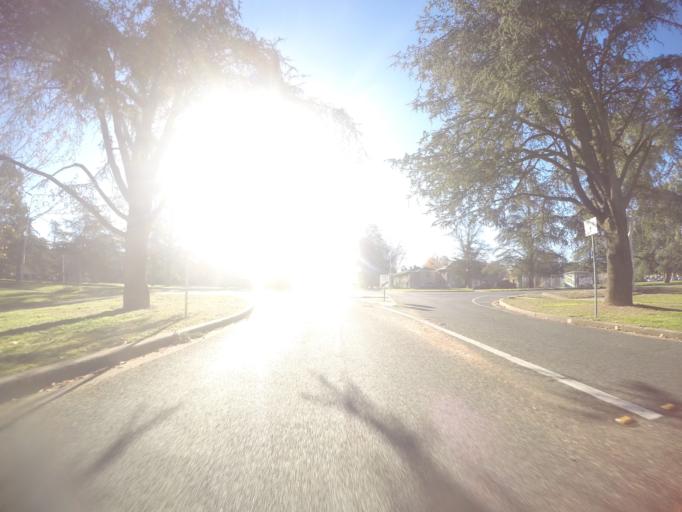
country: AU
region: Australian Capital Territory
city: Canberra
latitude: -35.2780
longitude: 149.1404
